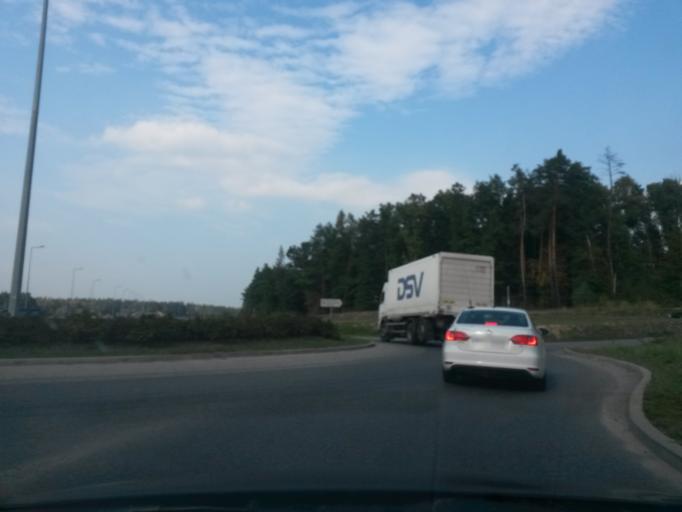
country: PL
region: Lesser Poland Voivodeship
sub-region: Powiat brzeski
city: Brzesko
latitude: 49.9885
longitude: 20.5922
